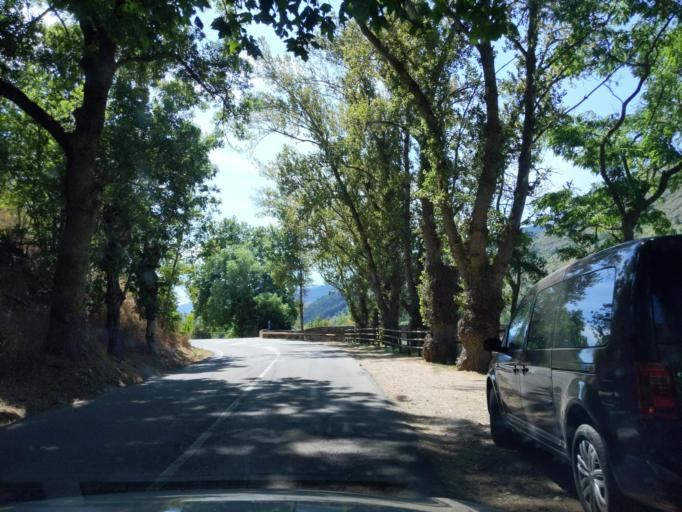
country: ES
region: La Rioja
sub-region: Provincia de La Rioja
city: Ezcaray
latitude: 42.3210
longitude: -3.0124
